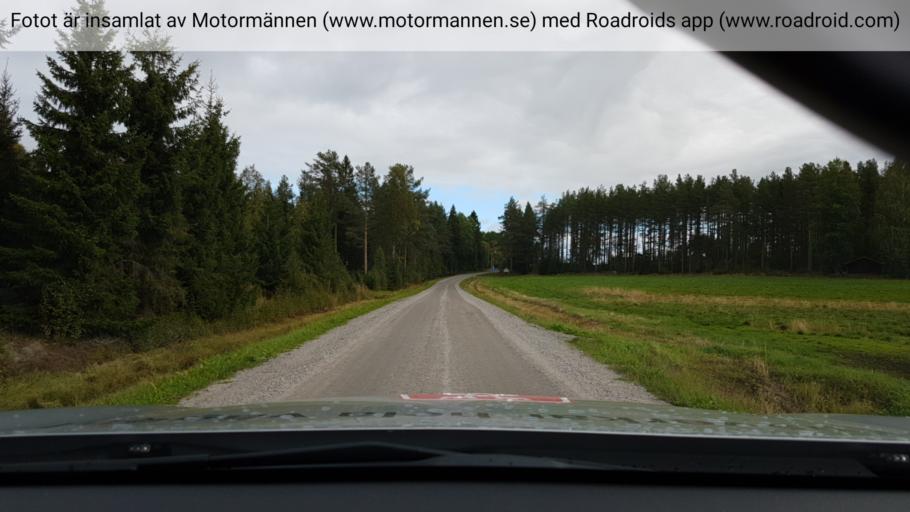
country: SE
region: Vaesterbotten
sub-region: Skelleftea Kommun
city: Byske
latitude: 65.1128
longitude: 21.1987
